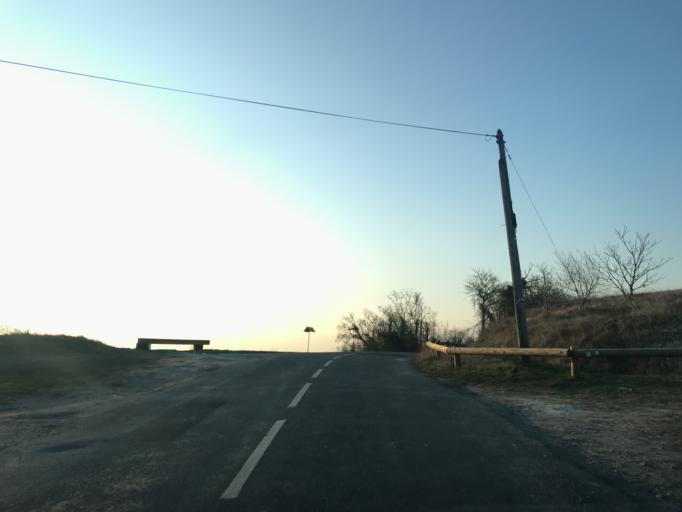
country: FR
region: Ile-de-France
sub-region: Departement des Yvelines
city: Freneuse
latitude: 49.0687
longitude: 1.6008
